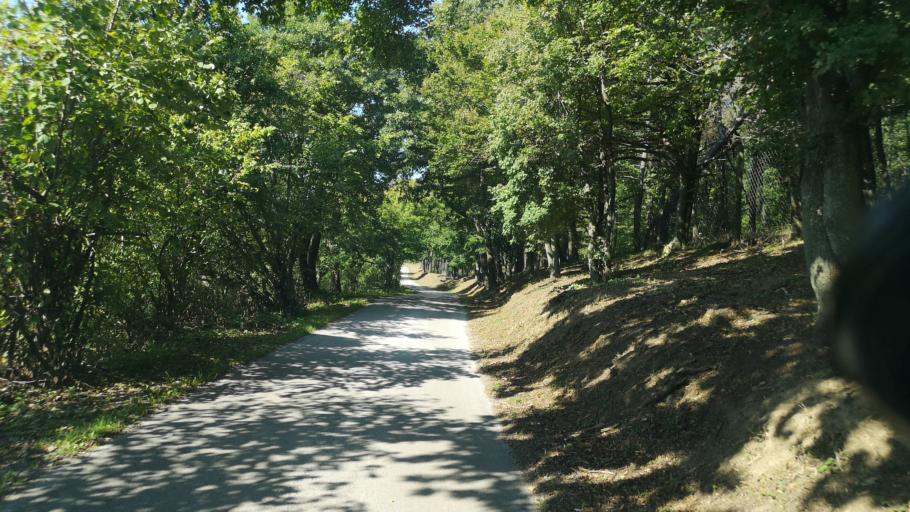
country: SK
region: Trnavsky
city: Smolenice
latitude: 48.5735
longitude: 17.4234
